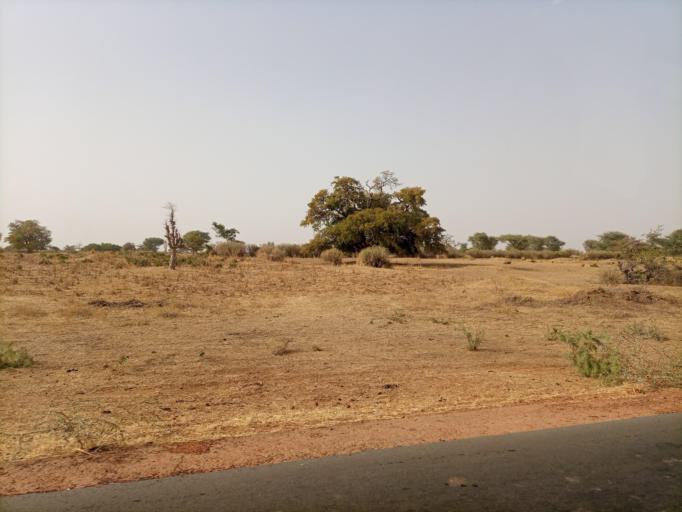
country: SN
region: Fatick
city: Foundiougne
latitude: 14.1230
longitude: -16.4267
